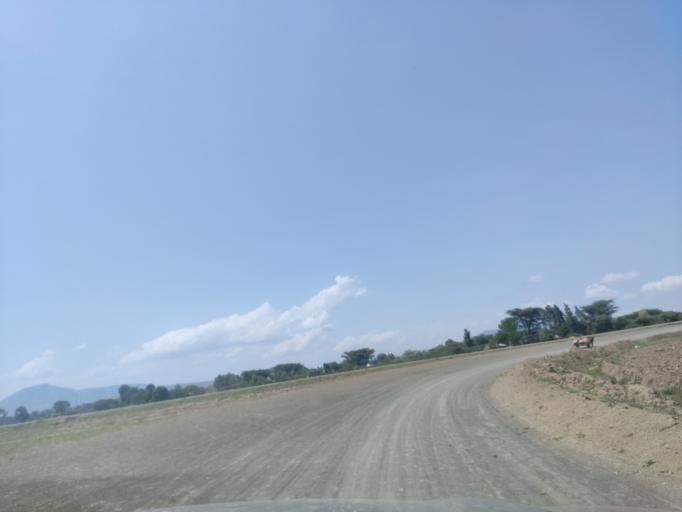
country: ET
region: Oromiya
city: Mojo
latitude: 8.3017
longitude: 38.9341
